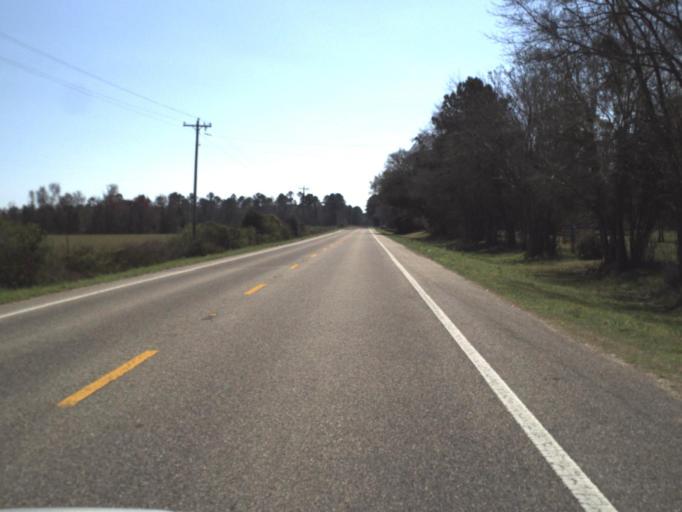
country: US
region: Florida
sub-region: Calhoun County
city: Blountstown
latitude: 30.5683
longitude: -85.0218
